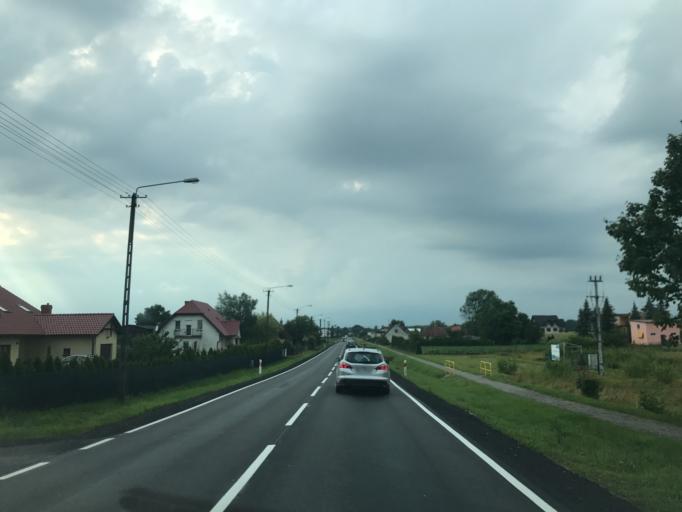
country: PL
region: Pomeranian Voivodeship
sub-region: Powiat czluchowski
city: Czluchow
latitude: 53.6800
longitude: 17.3381
